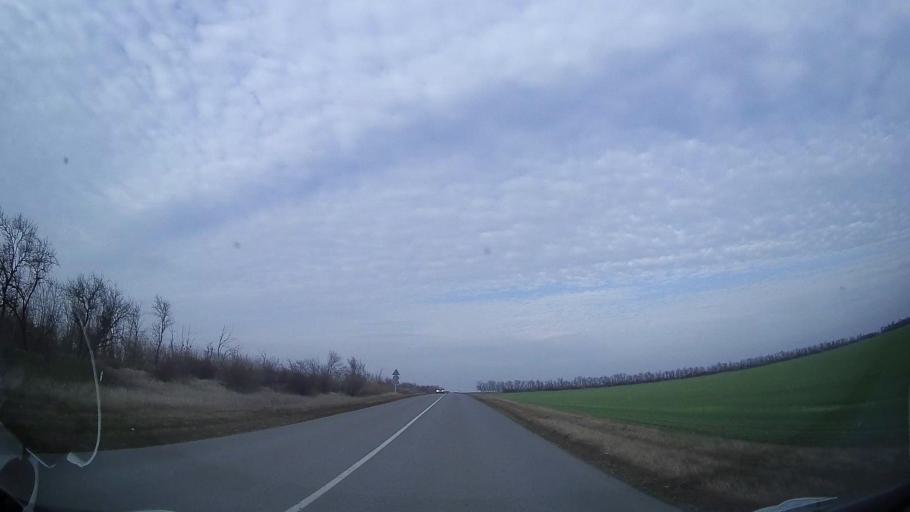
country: RU
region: Rostov
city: Zernograd
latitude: 46.9077
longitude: 40.3389
